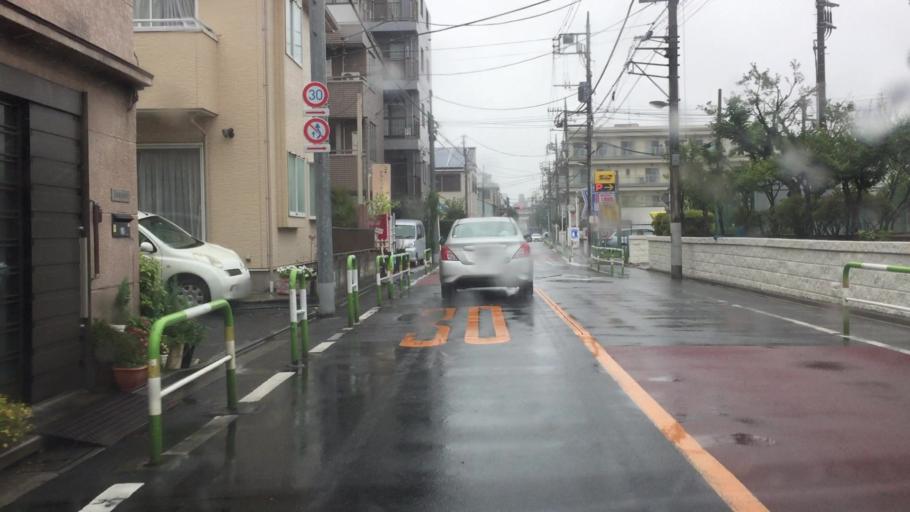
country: JP
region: Saitama
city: Soka
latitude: 35.7441
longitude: 139.7864
